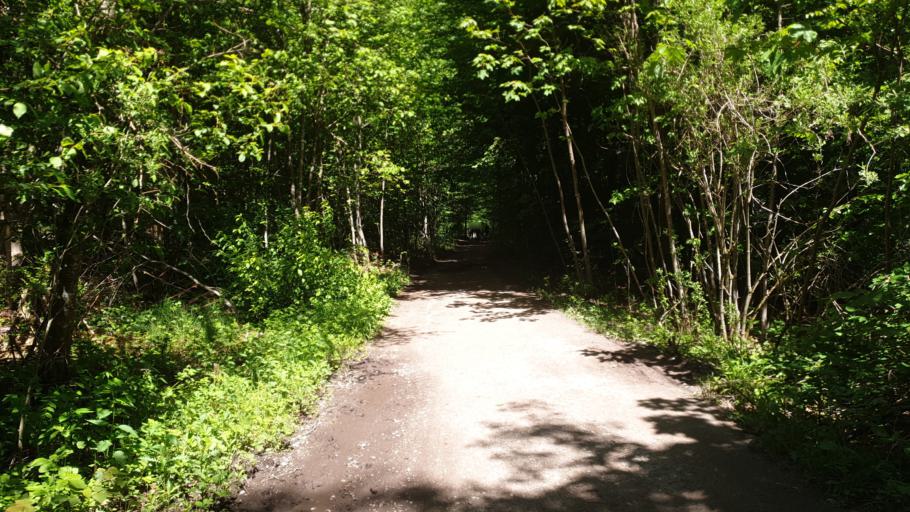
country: DE
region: Bavaria
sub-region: Upper Bavaria
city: Iffeldorf
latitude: 47.7867
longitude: 11.2963
